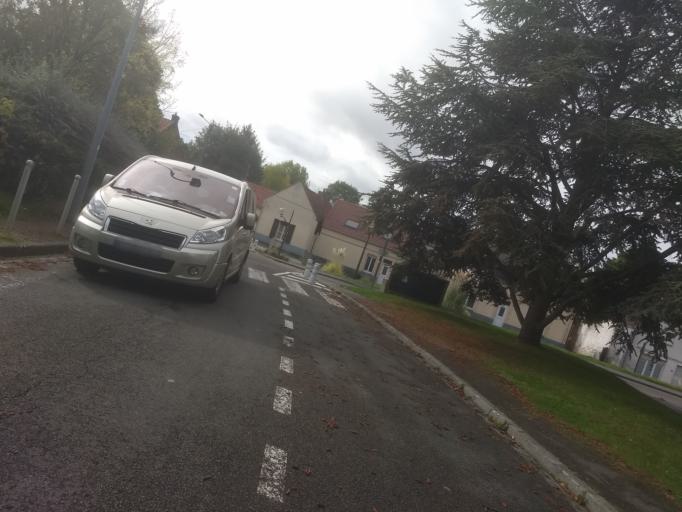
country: FR
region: Nord-Pas-de-Calais
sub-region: Departement du Pas-de-Calais
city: Anzin-Saint-Aubin
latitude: 50.3110
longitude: 2.7504
